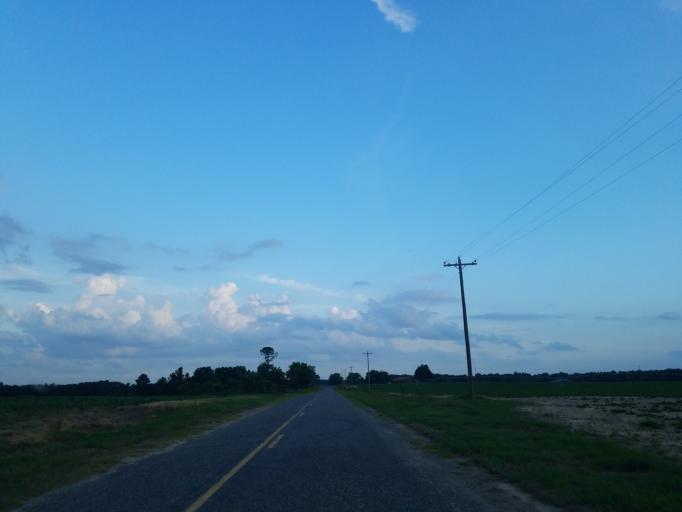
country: US
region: Georgia
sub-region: Dooly County
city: Unadilla
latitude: 32.1657
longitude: -83.7210
